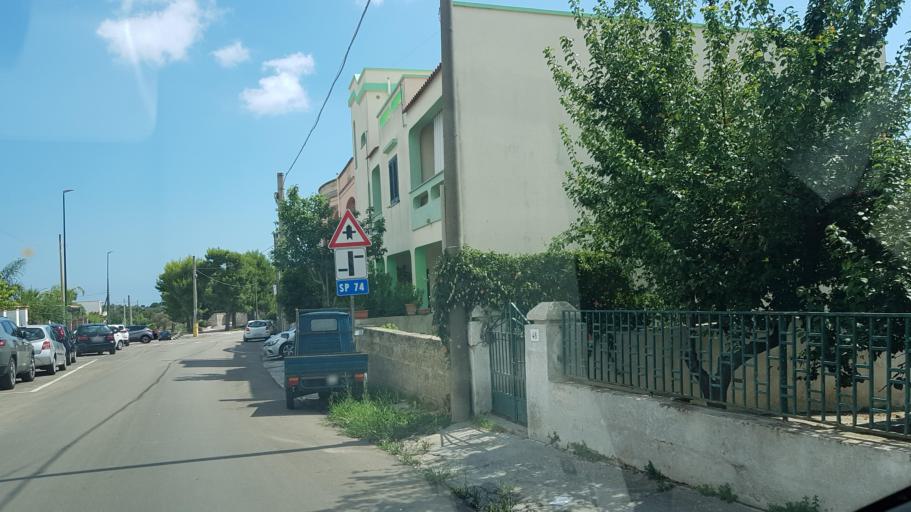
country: IT
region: Apulia
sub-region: Provincia di Lecce
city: Castrignano del Capo
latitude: 39.8303
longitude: 18.3523
